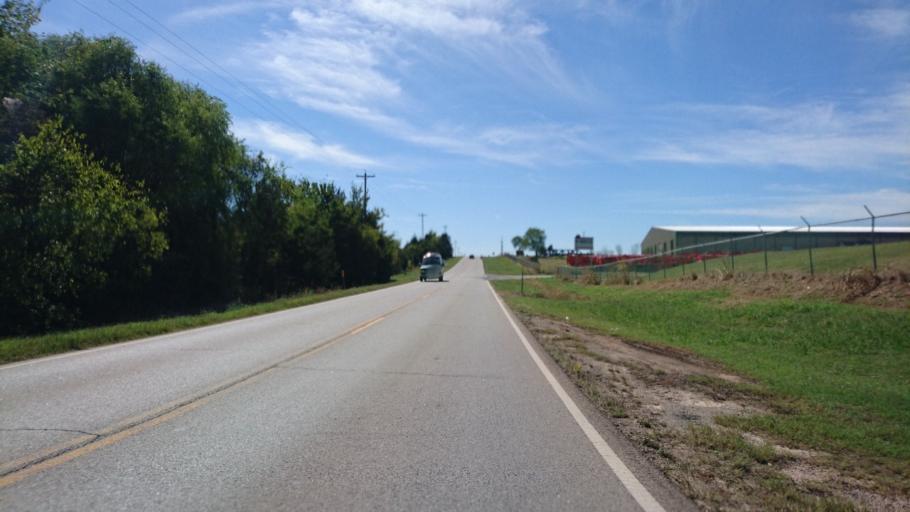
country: US
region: Oklahoma
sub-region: Lincoln County
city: Stroud
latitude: 35.7486
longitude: -96.6872
